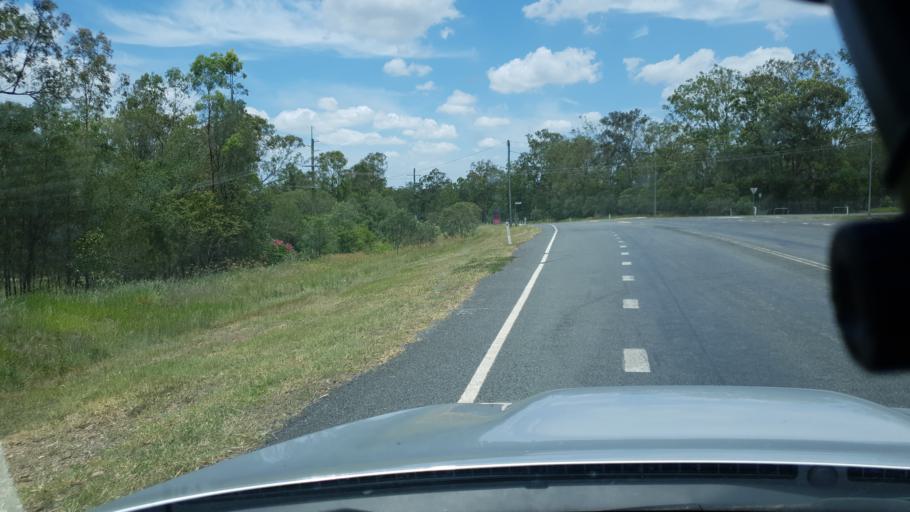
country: AU
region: Queensland
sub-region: Logan
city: North Maclean
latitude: -27.7734
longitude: 152.9811
